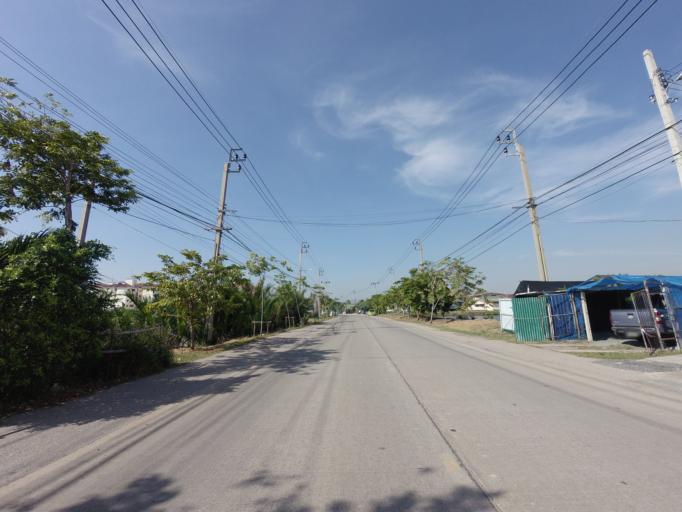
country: TH
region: Samut Prakan
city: Phra Samut Chedi
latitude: 13.5665
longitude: 100.5524
